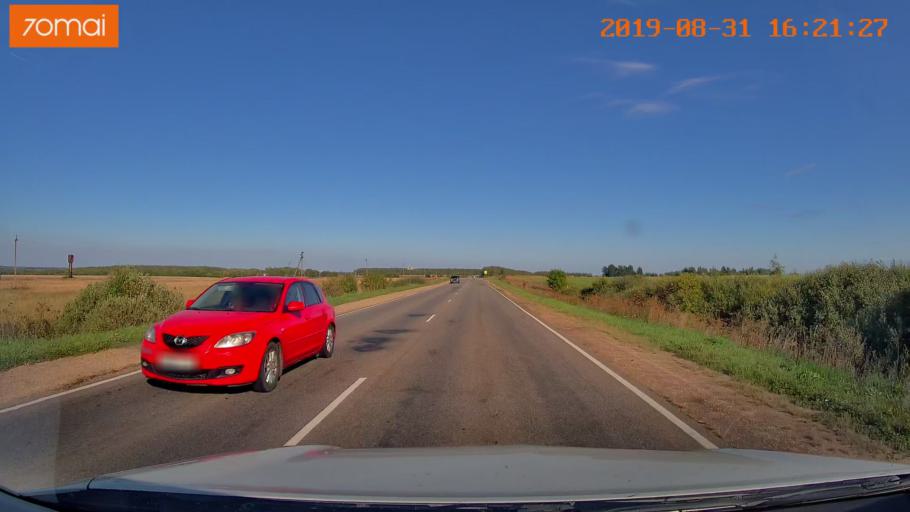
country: RU
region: Kaluga
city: Babynino
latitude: 54.5223
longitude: 35.6319
